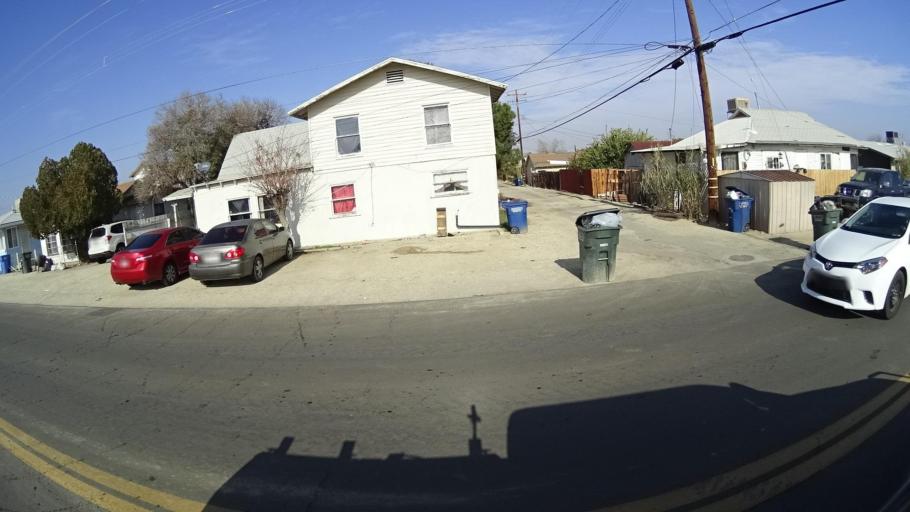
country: US
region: California
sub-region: Kern County
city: Ford City
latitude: 35.1543
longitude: -119.4635
